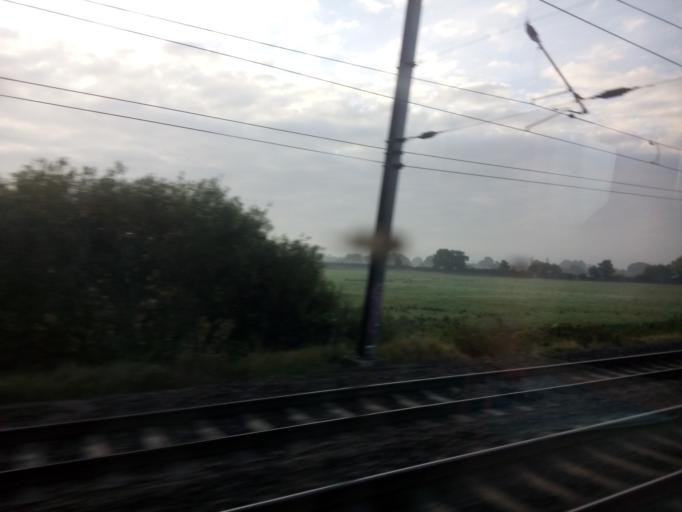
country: GB
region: England
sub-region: City of York
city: Copmanthorpe
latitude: 53.9229
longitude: -1.1262
